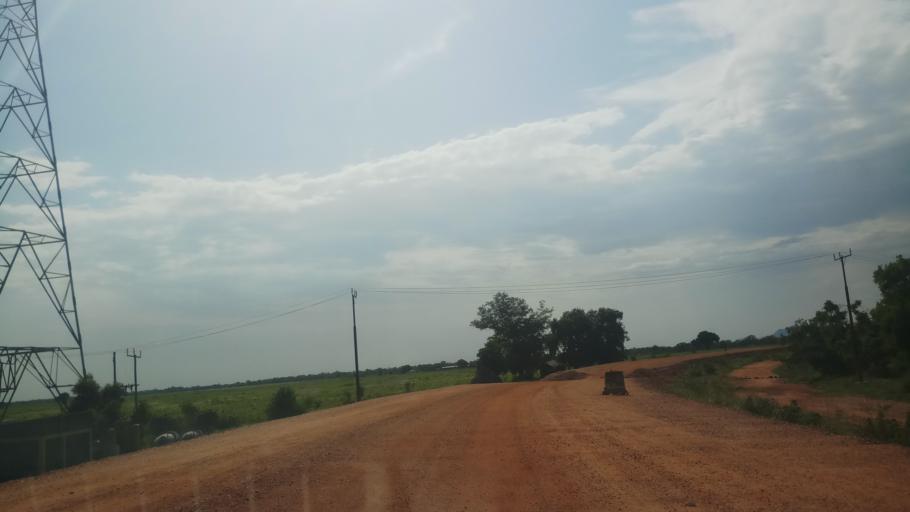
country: ET
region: Gambela
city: Gambela
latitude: 8.1565
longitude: 34.3368
